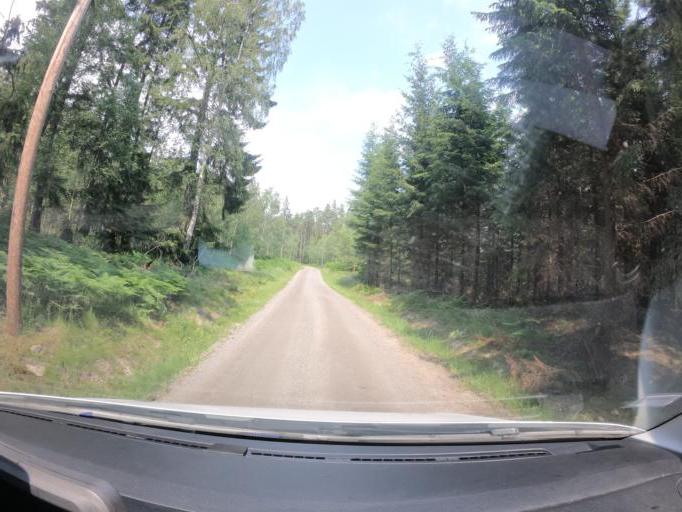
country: SE
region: Skane
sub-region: Hassleholms Kommun
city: Bjarnum
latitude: 56.3049
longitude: 13.5855
